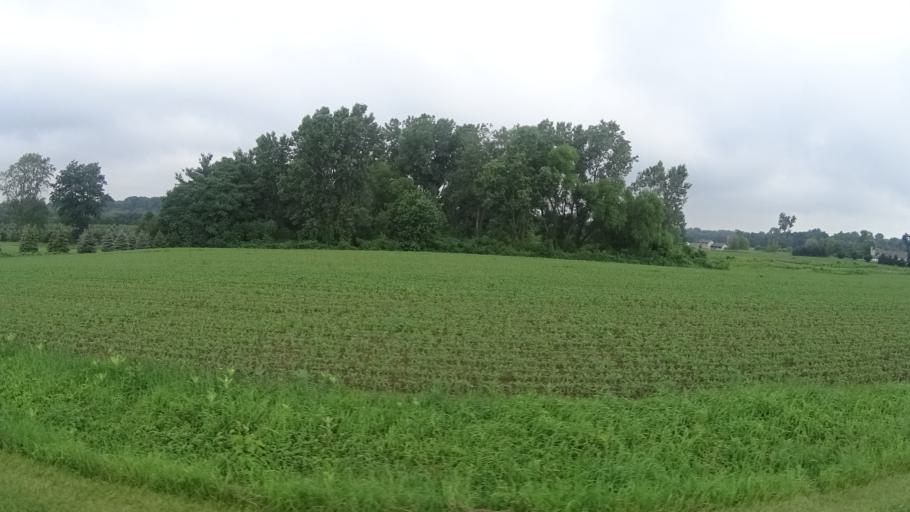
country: US
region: Ohio
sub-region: Erie County
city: Huron
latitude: 41.3126
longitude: -82.5032
